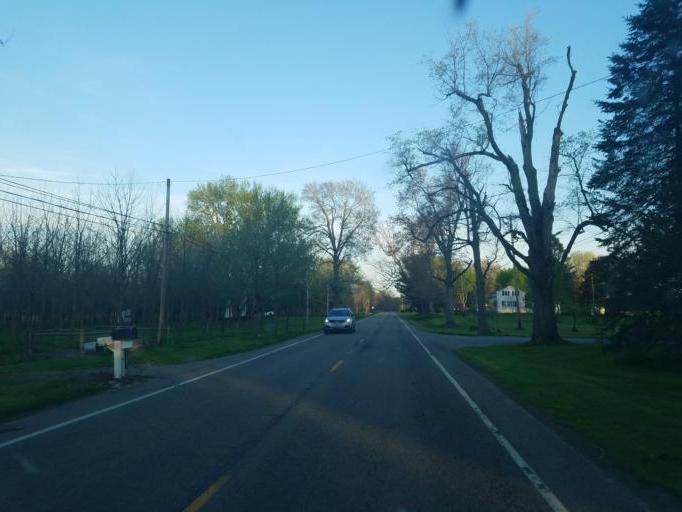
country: US
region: Ohio
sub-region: Trumbull County
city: Cortland
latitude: 41.4226
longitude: -80.5843
